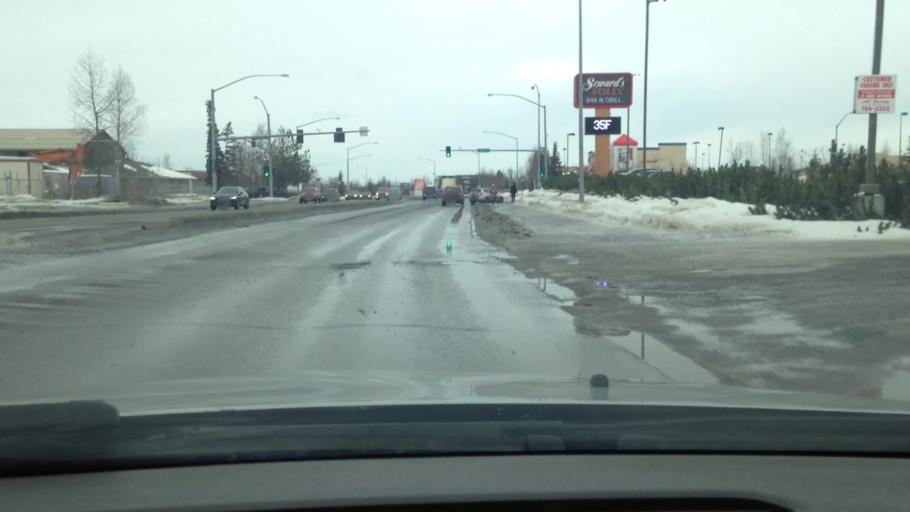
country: US
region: Alaska
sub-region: Anchorage Municipality
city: Anchorage
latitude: 61.1402
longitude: -149.8474
